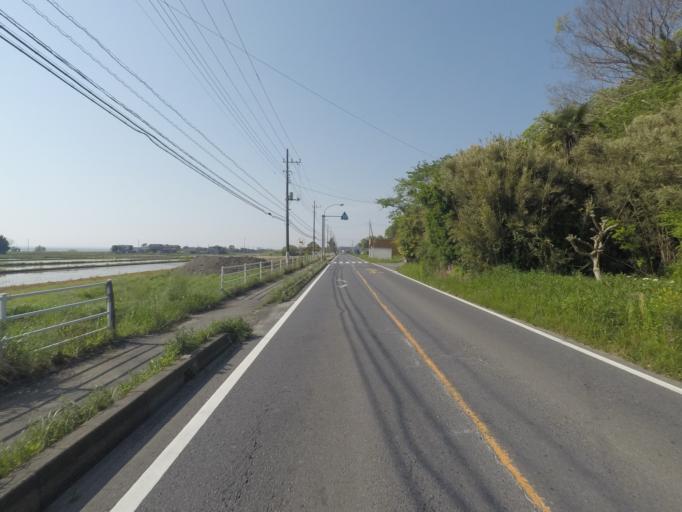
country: JP
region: Ibaraki
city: Itako
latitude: 36.0030
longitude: 140.4718
